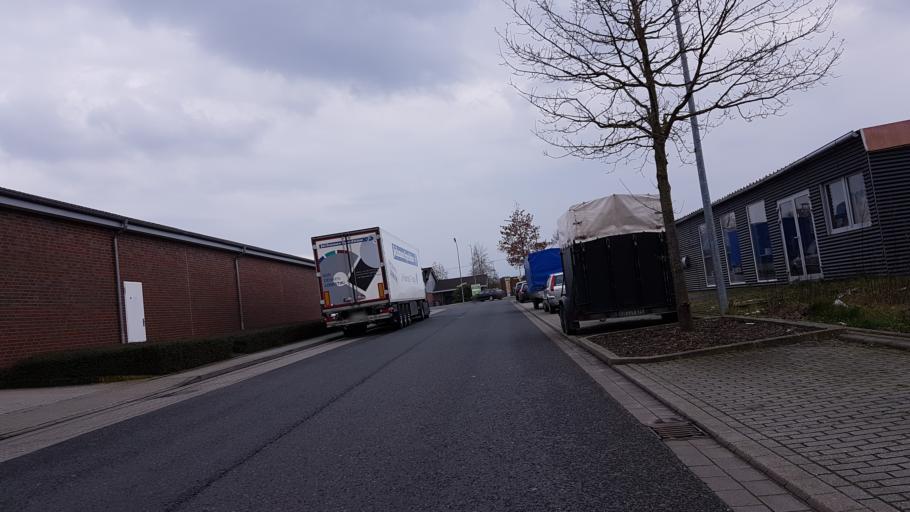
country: DE
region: North Rhine-Westphalia
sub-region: Regierungsbezirk Dusseldorf
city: Bruggen
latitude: 51.2107
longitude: 6.1811
